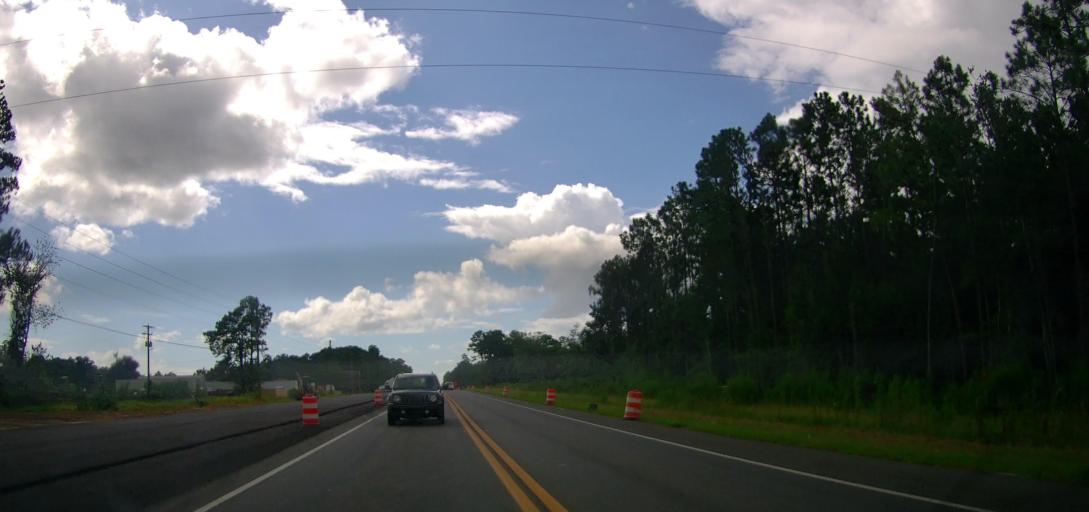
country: US
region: Georgia
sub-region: Coffee County
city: Douglas
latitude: 31.5230
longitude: -82.8968
